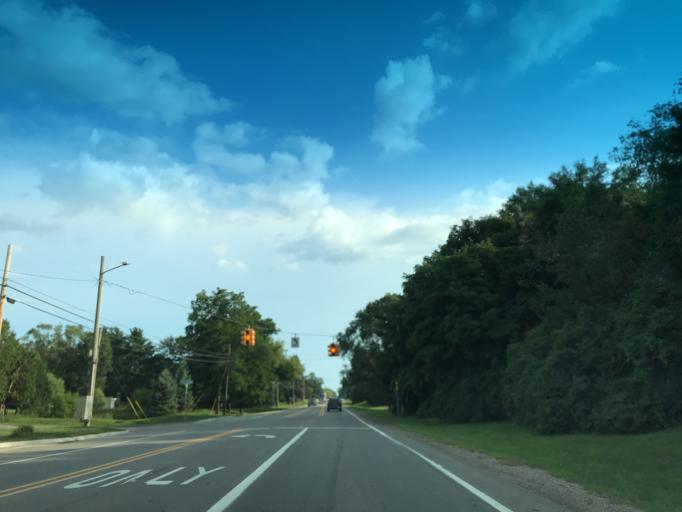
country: US
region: Michigan
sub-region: Oakland County
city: Milford
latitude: 42.5566
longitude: -83.6183
